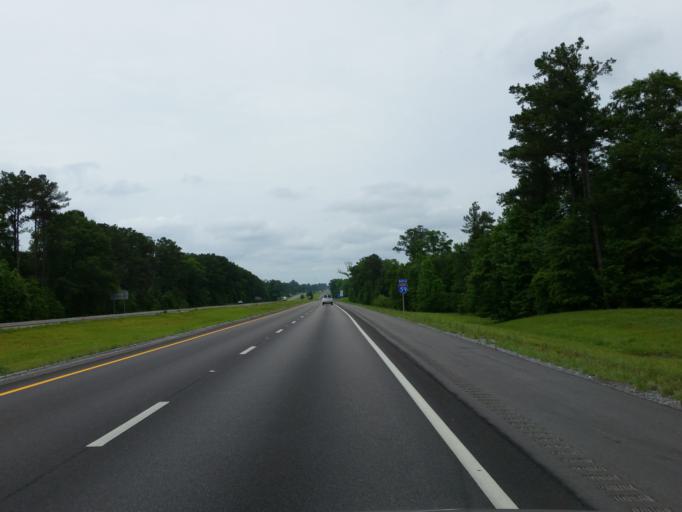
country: US
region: Mississippi
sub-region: Jones County
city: Sharon
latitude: 31.7898
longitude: -89.0546
